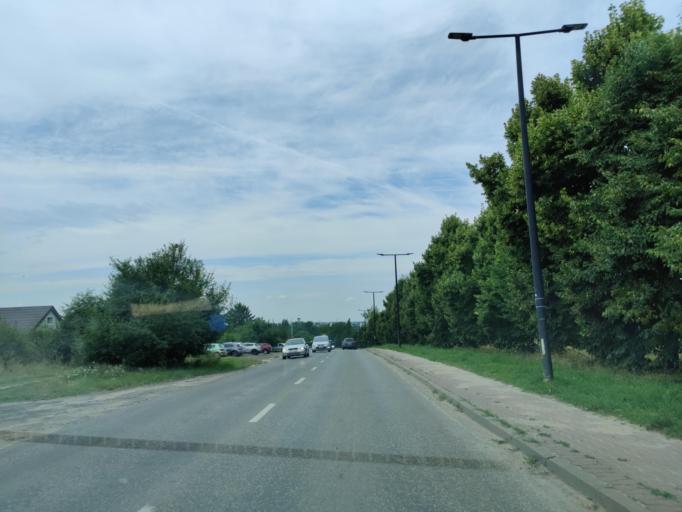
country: PL
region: Silesian Voivodeship
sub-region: Powiat bedzinski
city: Bedzin
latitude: 50.2882
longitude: 19.1645
